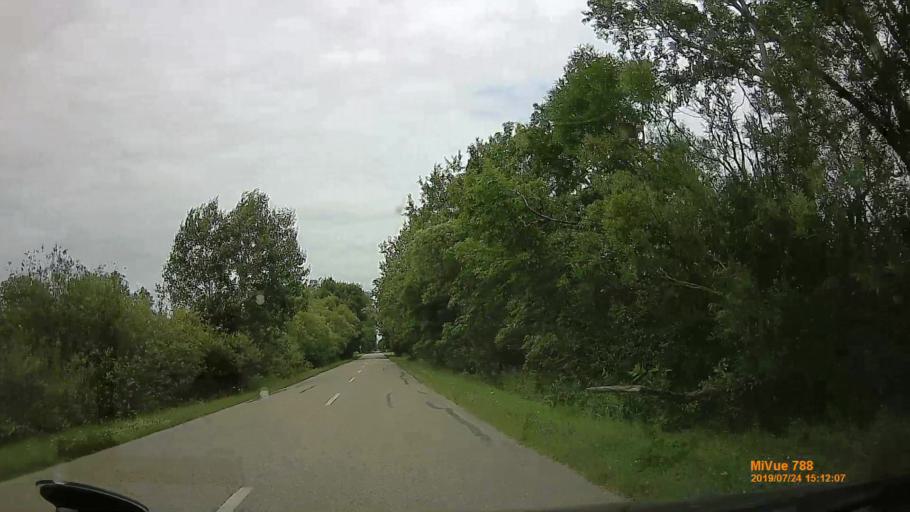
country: HU
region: Szabolcs-Szatmar-Bereg
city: Tarpa
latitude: 48.2015
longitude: 22.4904
